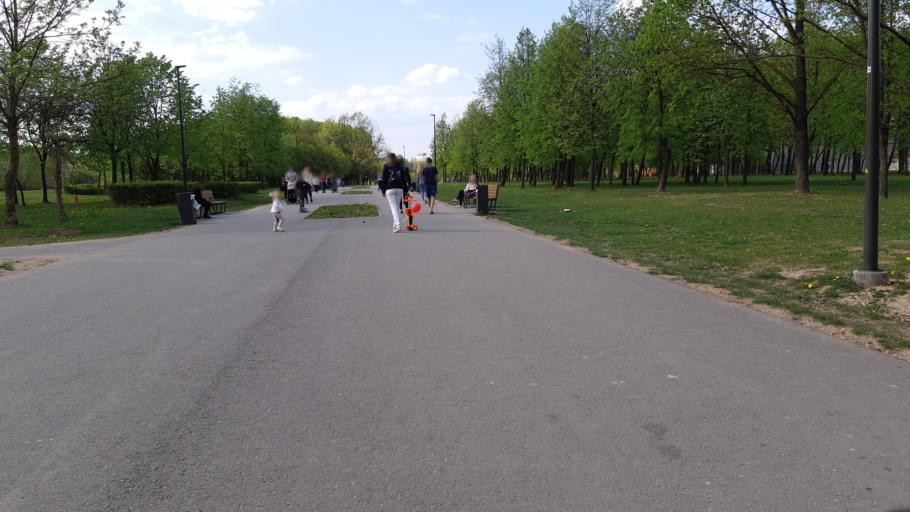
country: LT
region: Kauno apskritis
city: Dainava (Kaunas)
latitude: 54.9218
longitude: 23.9532
